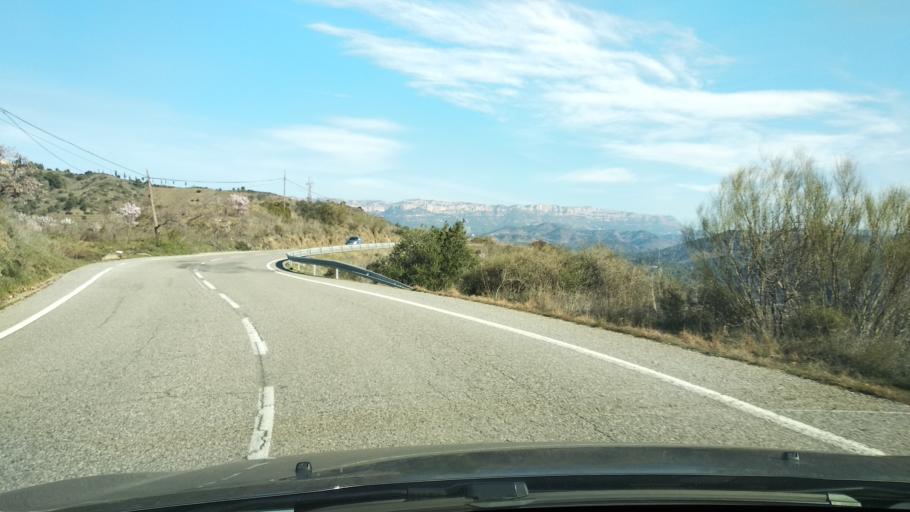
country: ES
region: Catalonia
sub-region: Provincia de Tarragona
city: Falset
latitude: 41.1973
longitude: 0.7805
